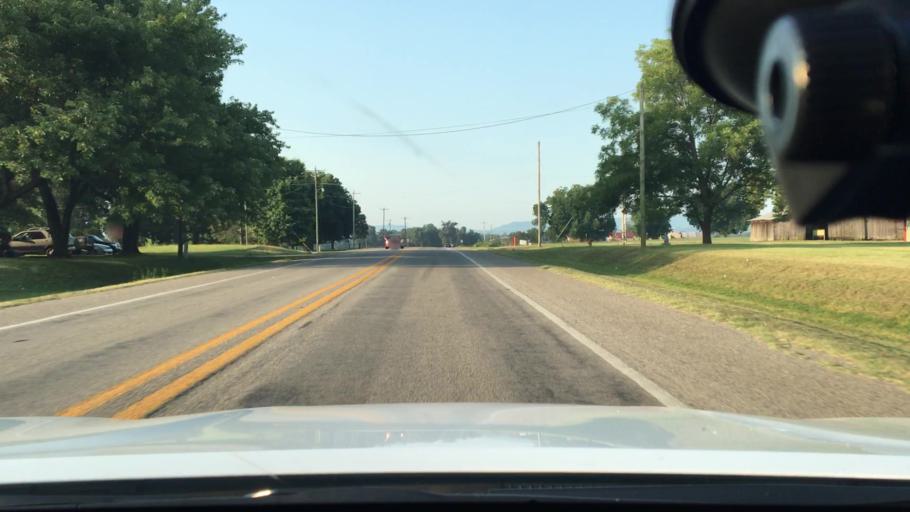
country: US
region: Arkansas
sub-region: Johnson County
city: Clarksville
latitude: 35.3851
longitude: -93.5297
